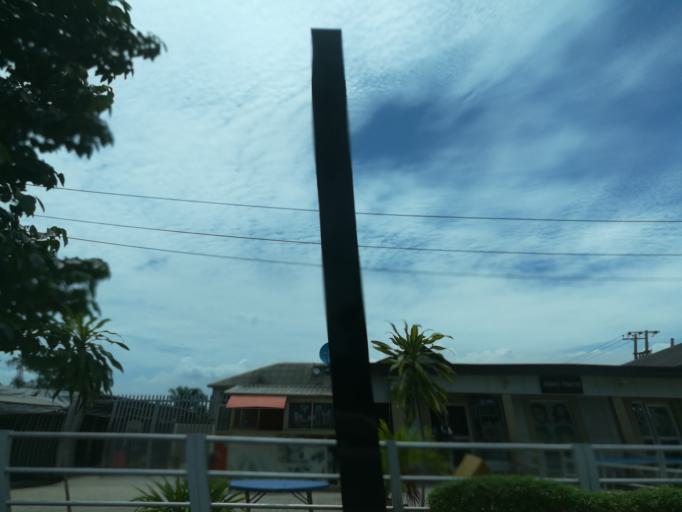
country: NG
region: Lagos
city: Ebute Ikorodu
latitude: 6.5867
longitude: 3.4925
